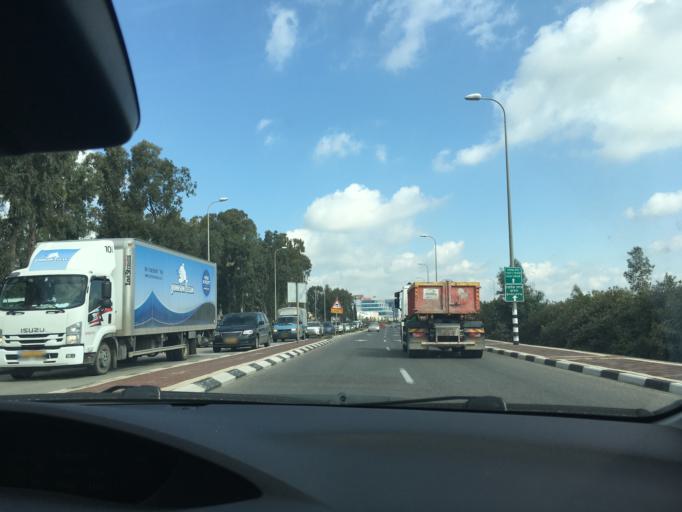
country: IL
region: Central District
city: Kfar Saba
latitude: 32.1714
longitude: 34.9300
